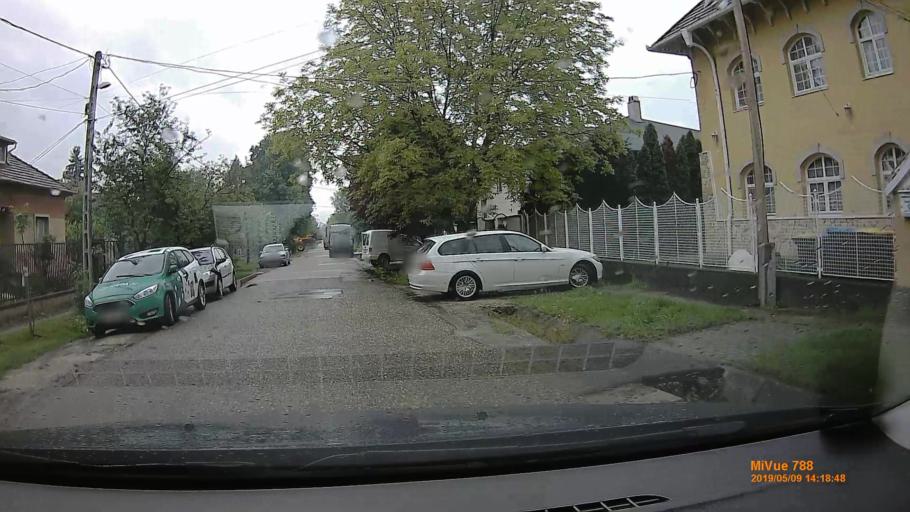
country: HU
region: Budapest
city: Budapest XVI. keruelet
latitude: 47.5043
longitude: 19.2070
